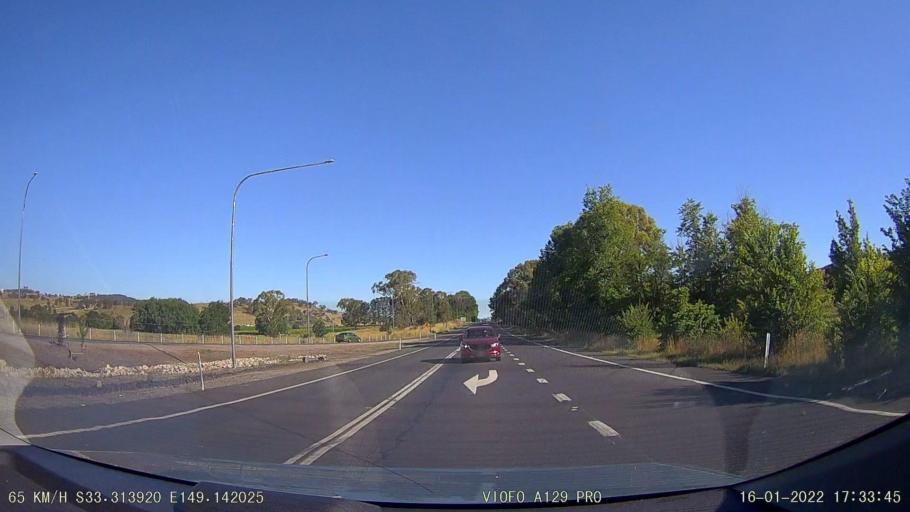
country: AU
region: New South Wales
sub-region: Orange Municipality
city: Orange
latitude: -33.3138
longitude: 149.1420
